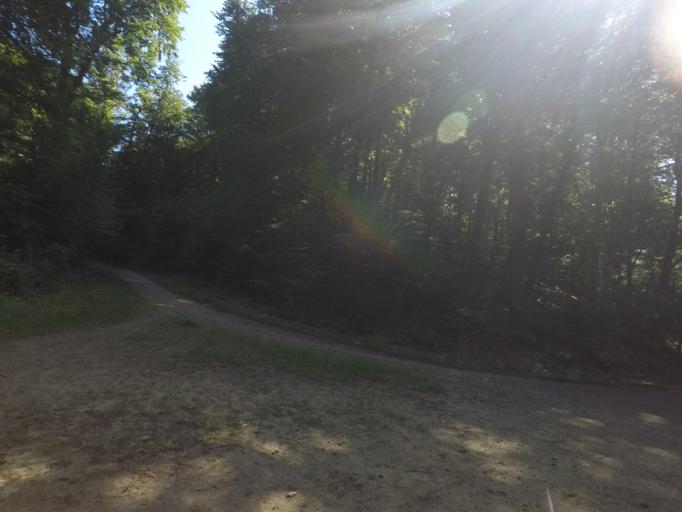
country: LU
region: Luxembourg
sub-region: Canton de Luxembourg
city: Bertrange
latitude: 49.6315
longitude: 6.0481
